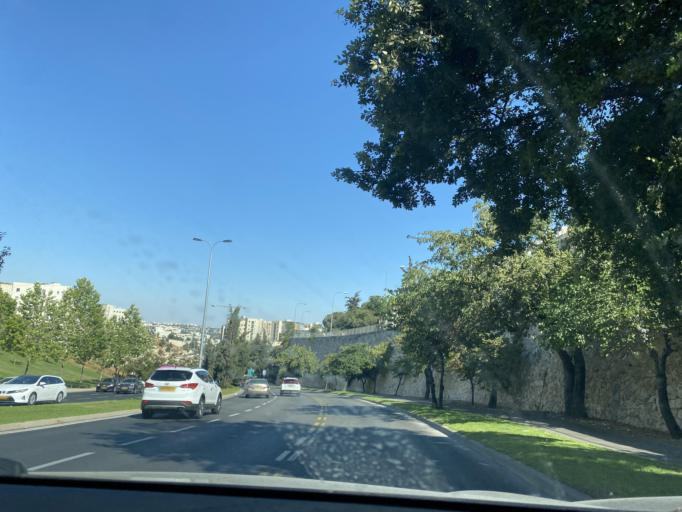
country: PS
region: West Bank
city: Bayt Iksa
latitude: 31.8204
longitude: 35.1900
